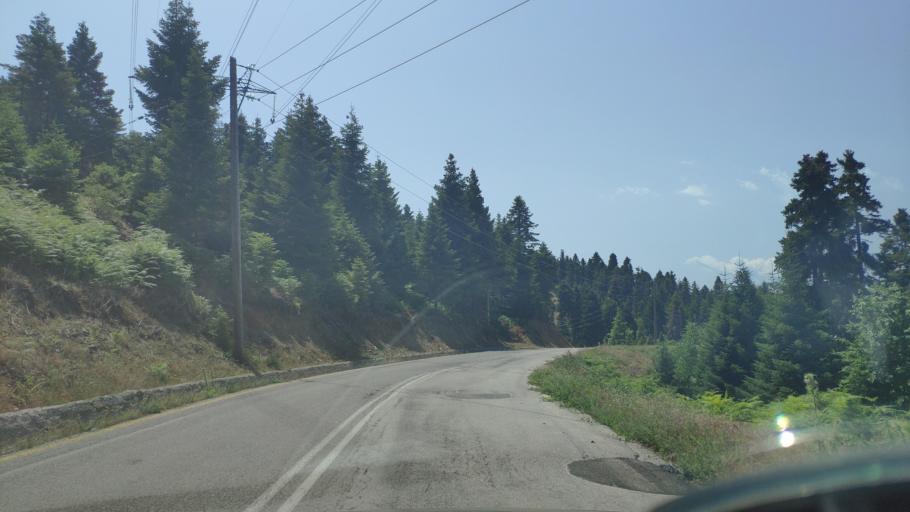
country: GR
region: Epirus
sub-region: Nomos Artas
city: Ano Kalentini
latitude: 39.2673
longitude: 21.2680
